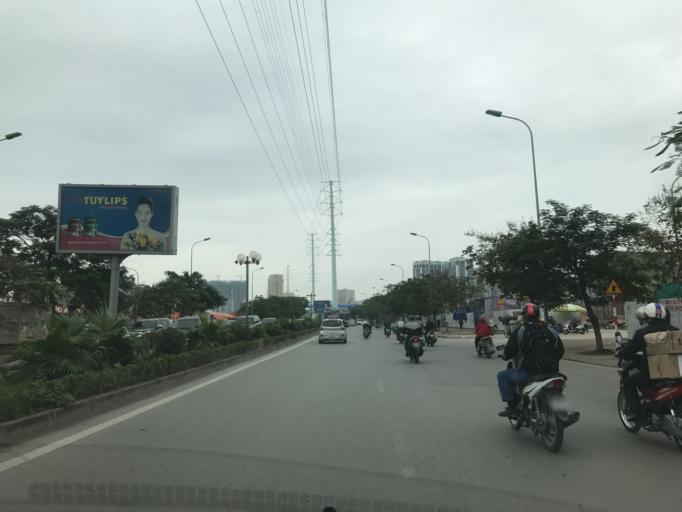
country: VN
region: Ha Noi
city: Ha Dong
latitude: 20.9838
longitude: 105.7729
